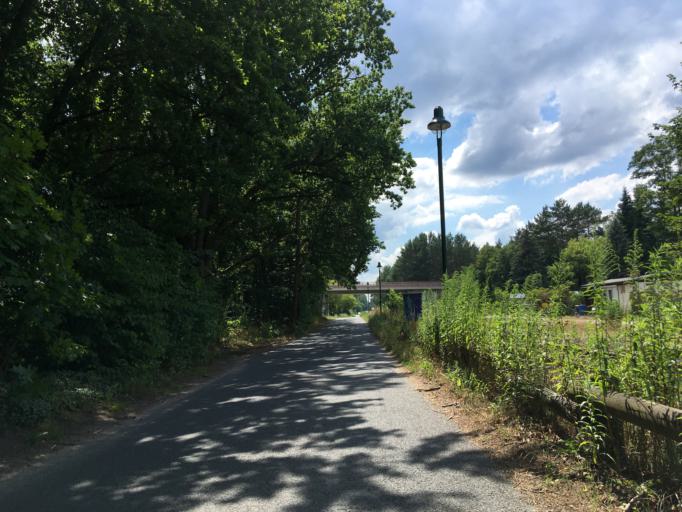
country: DE
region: Brandenburg
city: Wandlitz
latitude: 52.7422
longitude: 13.4634
